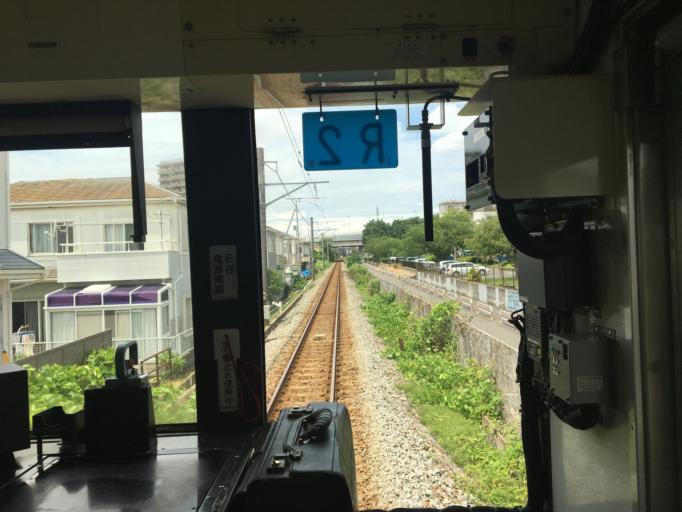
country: JP
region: Kanagawa
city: Chigasaki
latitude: 35.3485
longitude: 139.4026
